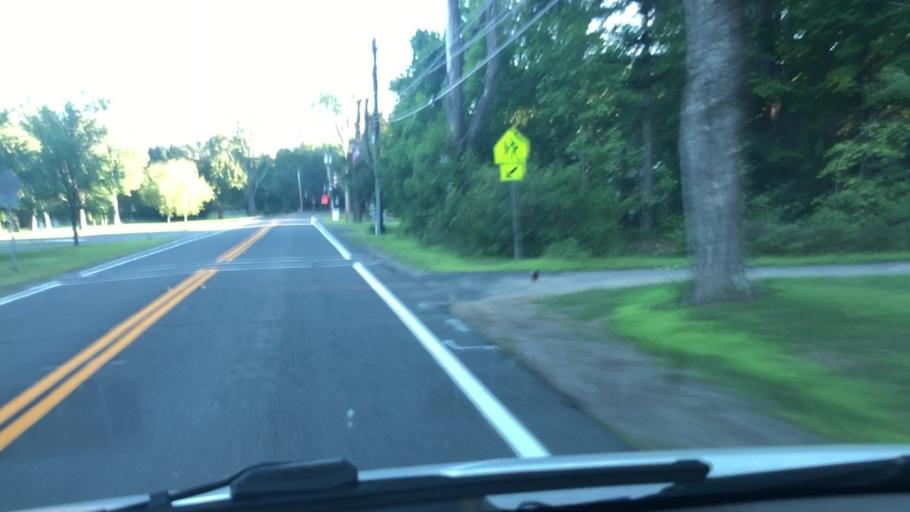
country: US
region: Massachusetts
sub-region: Hampshire County
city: Chesterfield
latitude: 42.4000
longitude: -72.9375
